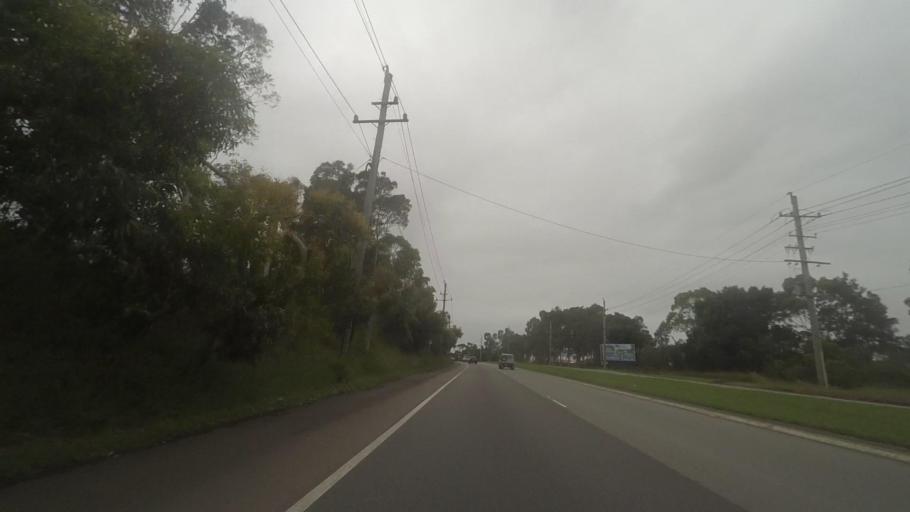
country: AU
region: New South Wales
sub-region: Newcastle
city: Mayfield West
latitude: -32.8773
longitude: 151.7145
